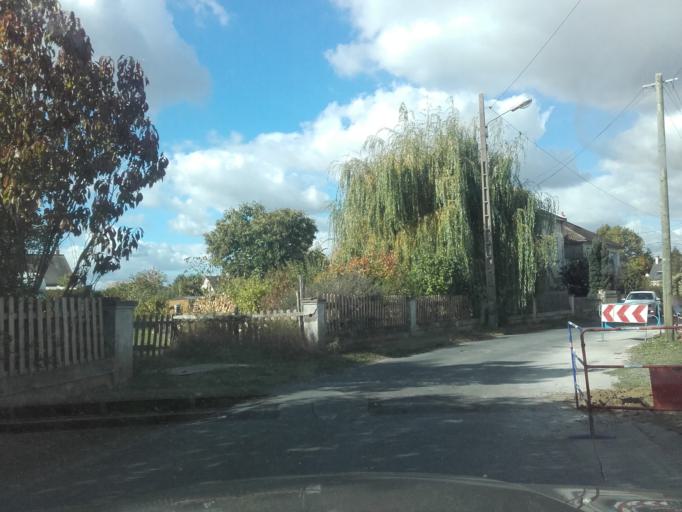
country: FR
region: Centre
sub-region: Departement d'Indre-et-Loire
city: La Ville-aux-Dames
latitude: 47.3974
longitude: 0.7561
